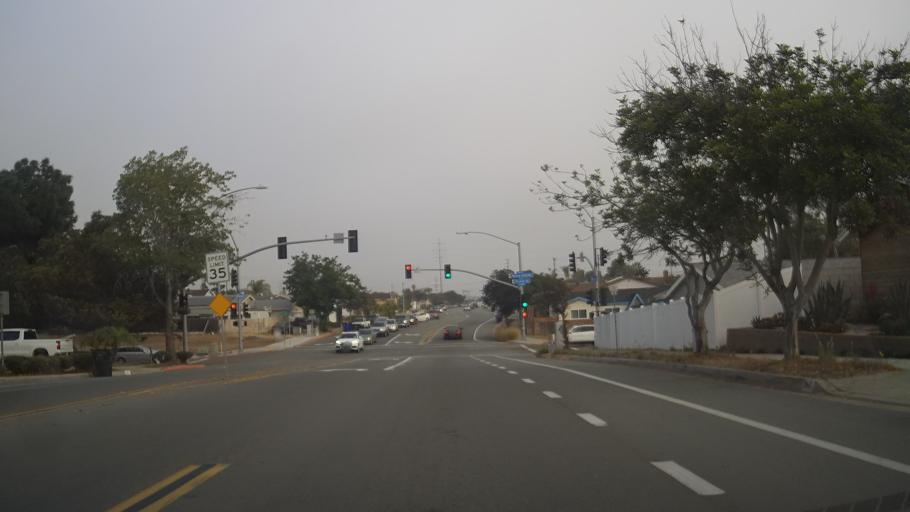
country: US
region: California
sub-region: San Diego County
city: San Diego
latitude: 32.7892
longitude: -117.1448
